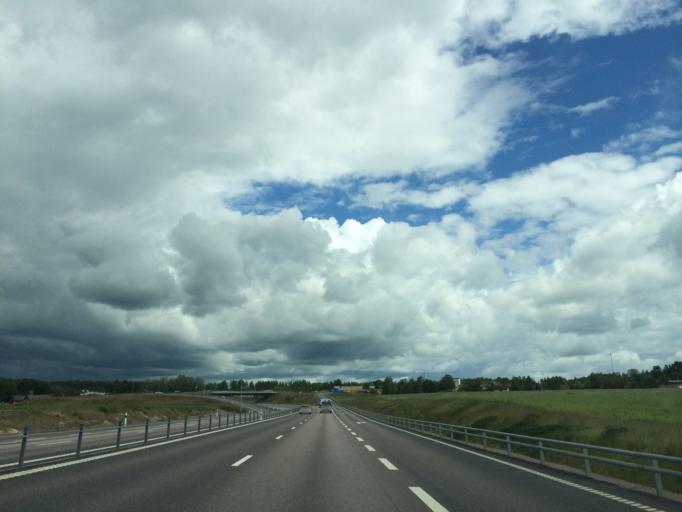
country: SE
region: OEstergoetland
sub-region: Mjolby Kommun
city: Mjolby
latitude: 58.3347
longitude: 15.0989
